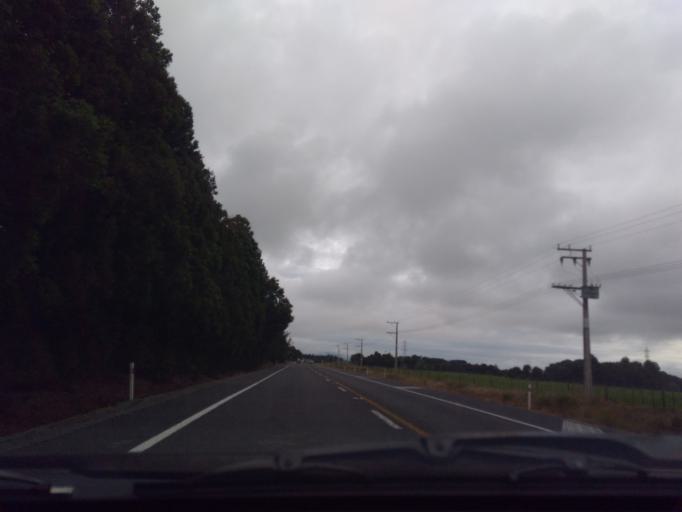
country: NZ
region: Northland
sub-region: Whangarei
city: Ruakaka
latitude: -35.9959
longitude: 174.4192
